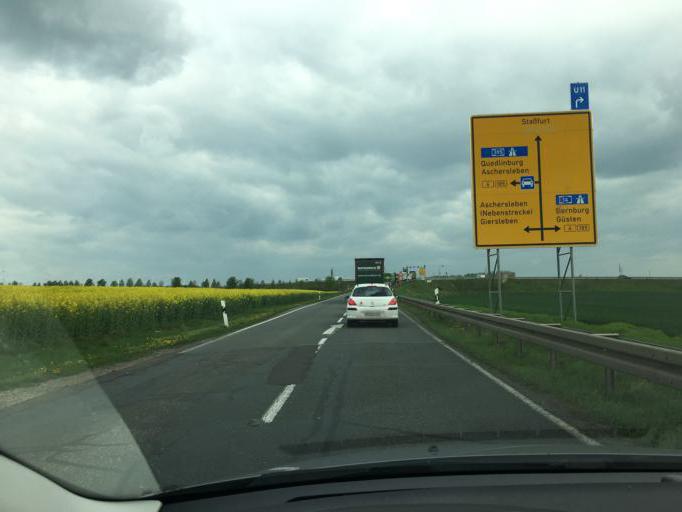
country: DE
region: Saxony-Anhalt
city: Giersleben
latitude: 51.7841
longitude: 11.5737
